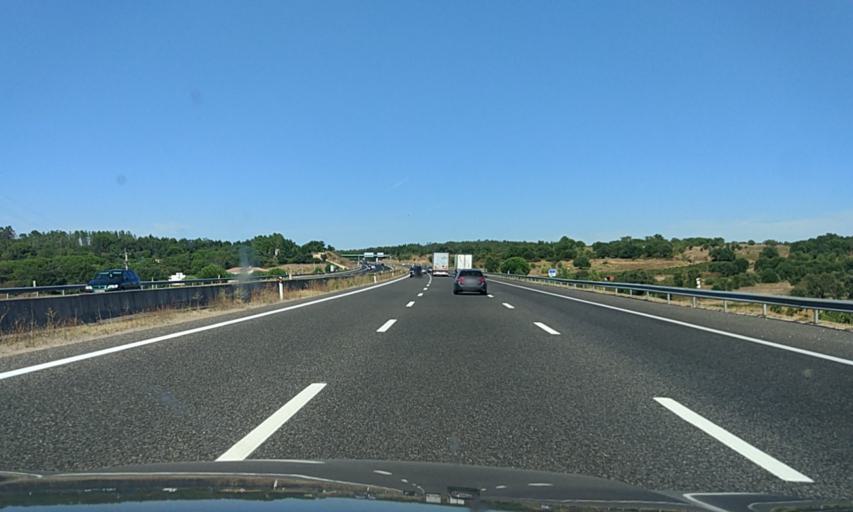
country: PT
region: Santarem
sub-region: Cartaxo
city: Cartaxo
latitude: 39.2120
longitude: -8.7818
